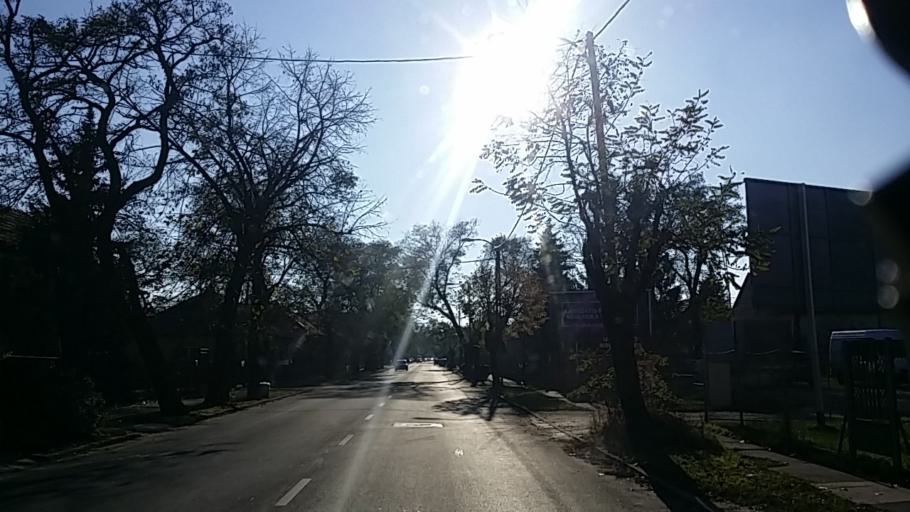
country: HU
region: Budapest
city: Budapest XVIII. keruelet
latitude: 47.4445
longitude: 19.1899
